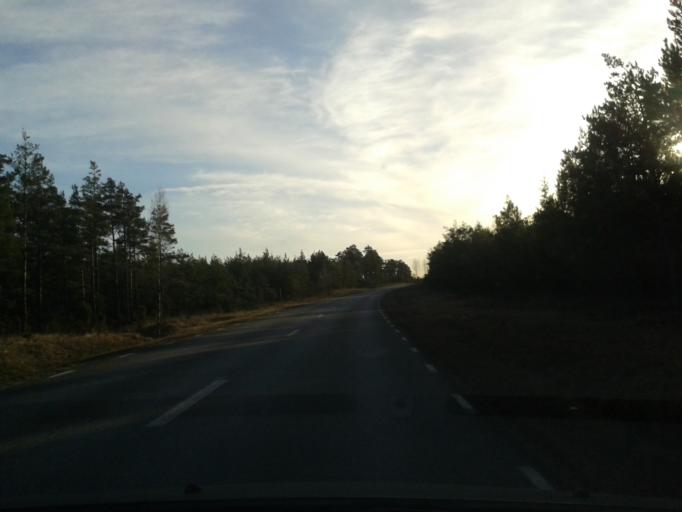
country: SE
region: Gotland
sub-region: Gotland
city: Hemse
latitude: 57.4079
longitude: 18.6355
